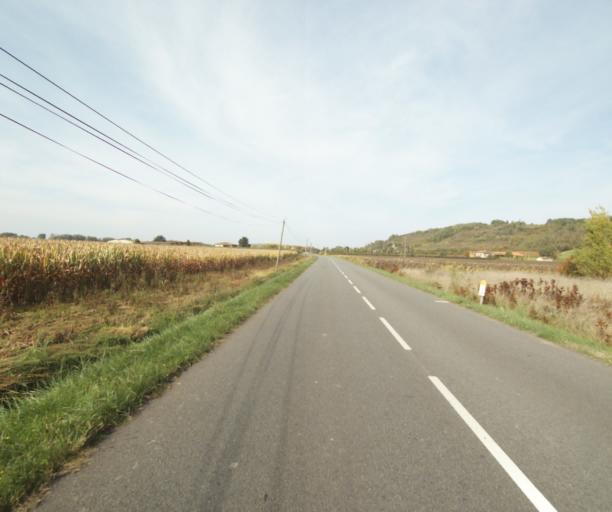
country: FR
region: Midi-Pyrenees
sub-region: Departement du Tarn-et-Garonne
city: Corbarieu
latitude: 43.9331
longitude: 1.3807
